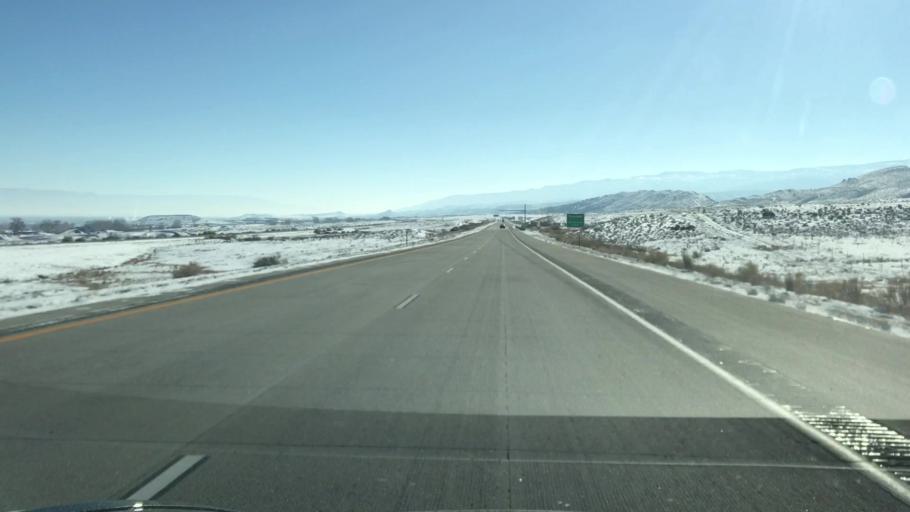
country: US
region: Colorado
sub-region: Mesa County
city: Loma
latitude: 39.1883
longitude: -108.8381
